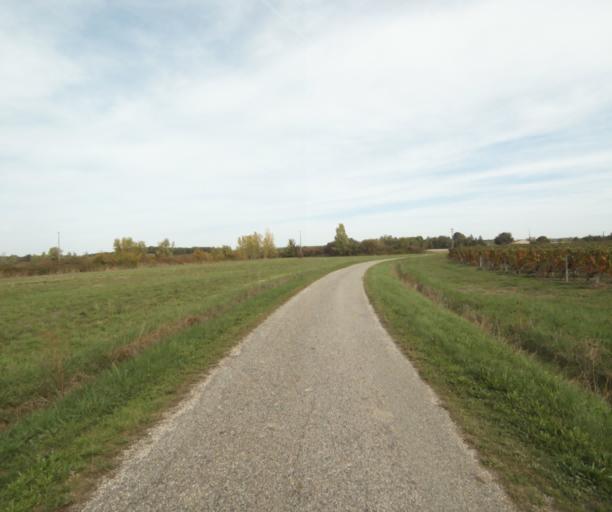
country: FR
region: Midi-Pyrenees
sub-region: Departement du Tarn-et-Garonne
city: Orgueil
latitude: 43.8915
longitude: 1.3961
